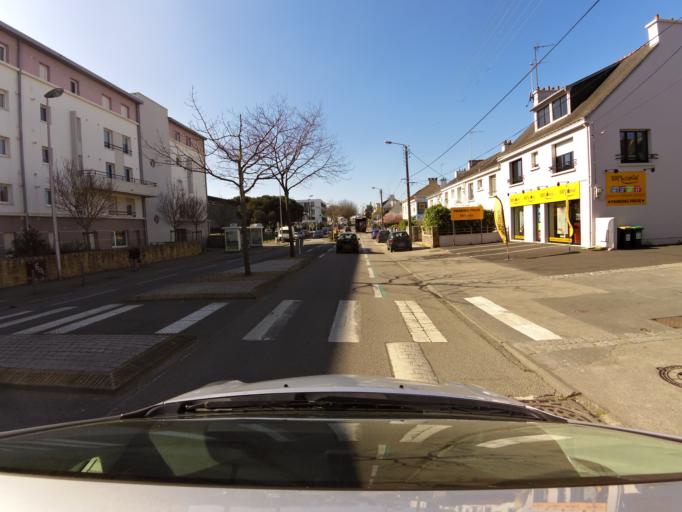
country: FR
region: Brittany
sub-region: Departement du Morbihan
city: Lorient
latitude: 47.7374
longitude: -3.3824
